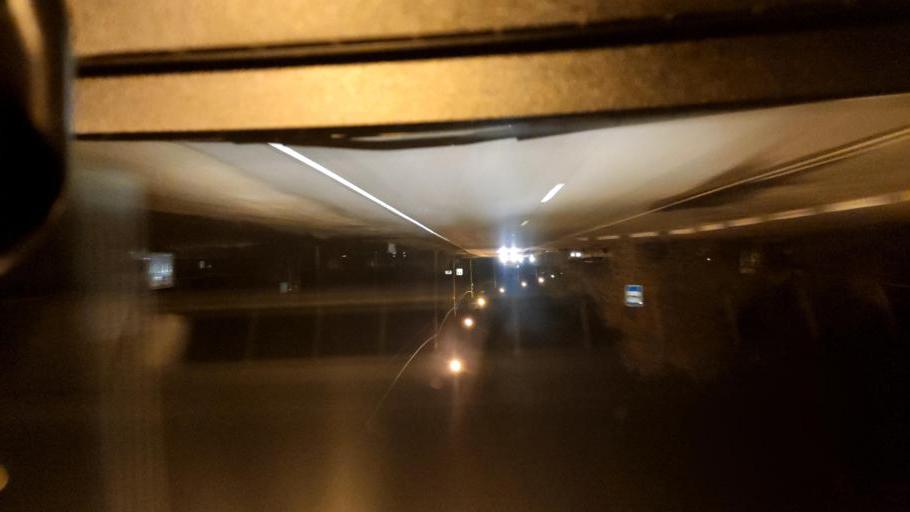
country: RU
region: Voronezj
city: Shilovo
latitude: 51.5674
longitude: 39.0479
